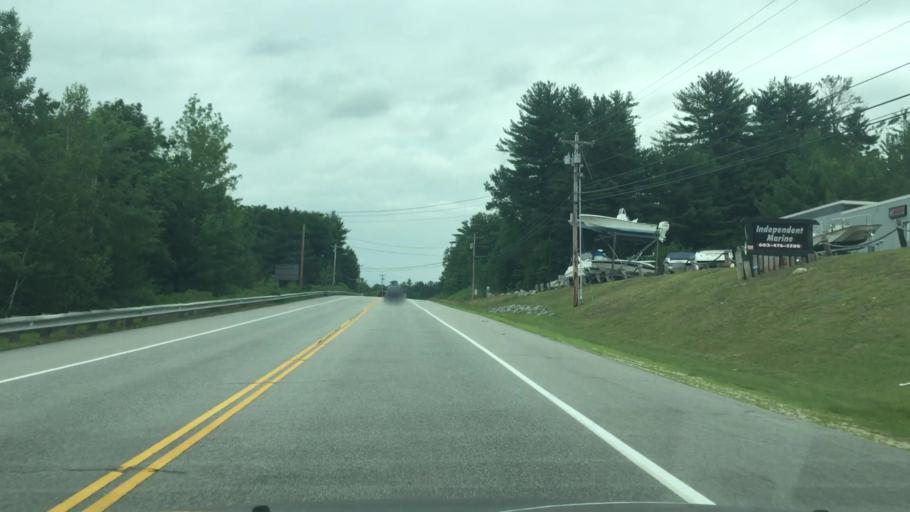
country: US
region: New Hampshire
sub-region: Carroll County
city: Moultonborough
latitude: 43.7646
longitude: -71.3858
